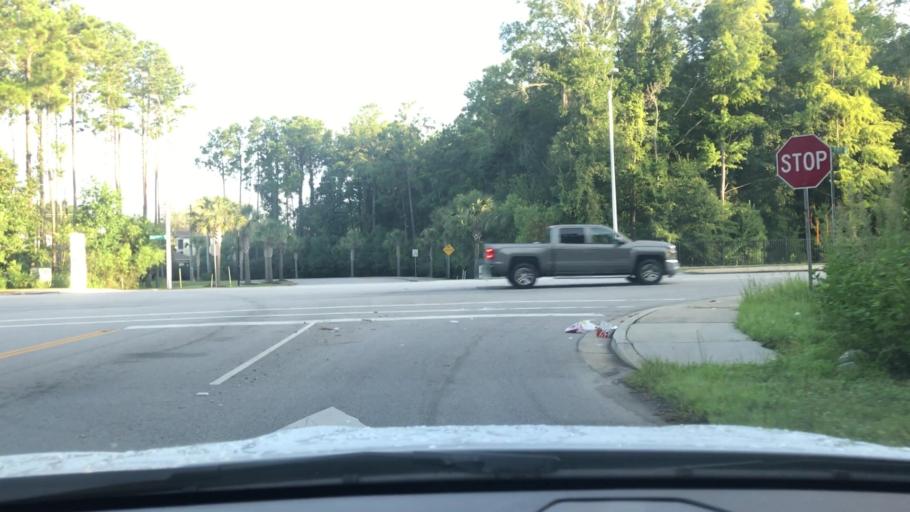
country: US
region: South Carolina
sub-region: Charleston County
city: Shell Point
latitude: 32.8194
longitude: -80.0923
